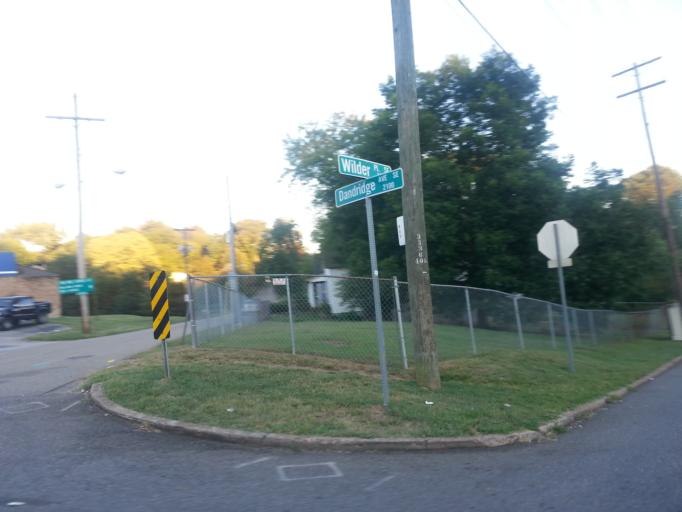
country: US
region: Tennessee
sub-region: Knox County
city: Knoxville
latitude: 35.9724
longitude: -83.8926
